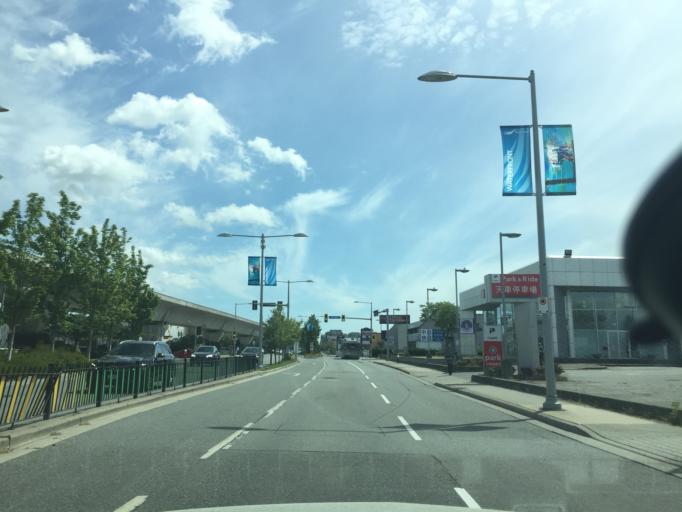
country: CA
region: British Columbia
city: Richmond
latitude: 49.1839
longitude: -123.1367
